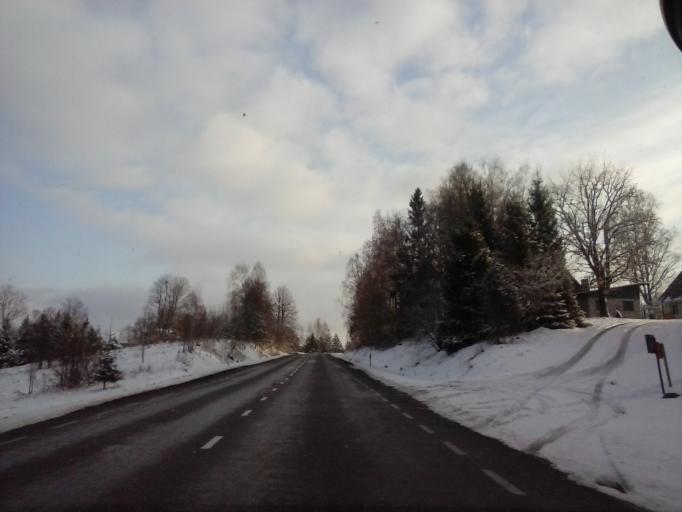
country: EE
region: Tartu
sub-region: Tartu linn
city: Tartu
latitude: 58.3496
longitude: 26.9110
